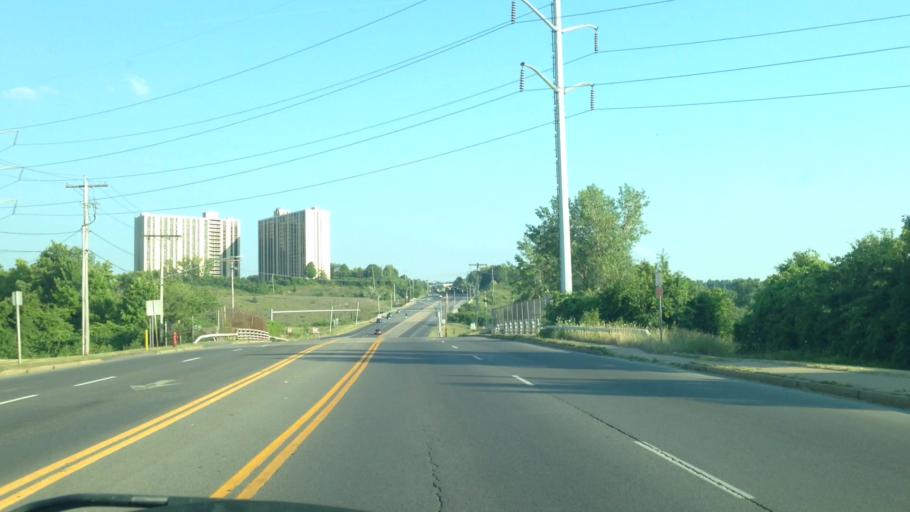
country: US
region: New York
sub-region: Onondaga County
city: Nedrow
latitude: 43.0107
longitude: -76.1337
